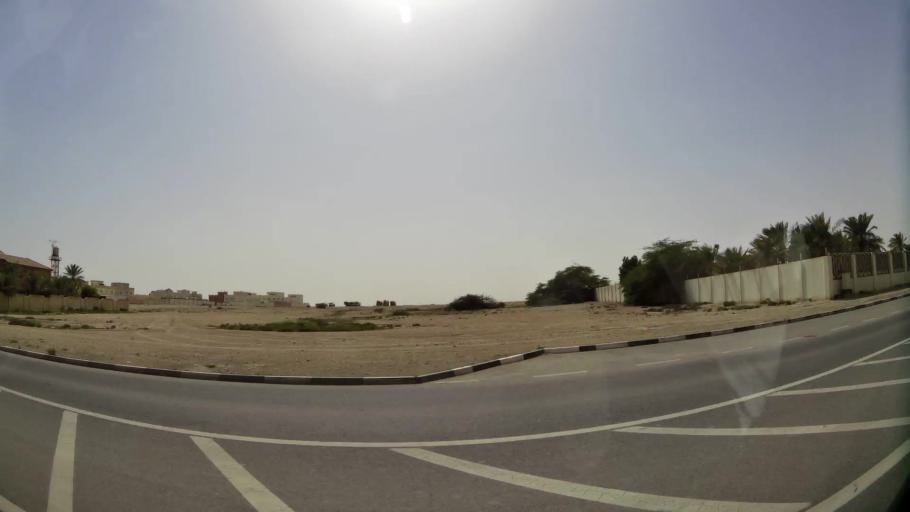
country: QA
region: Baladiyat Umm Salal
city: Umm Salal Muhammad
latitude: 25.4039
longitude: 51.4190
